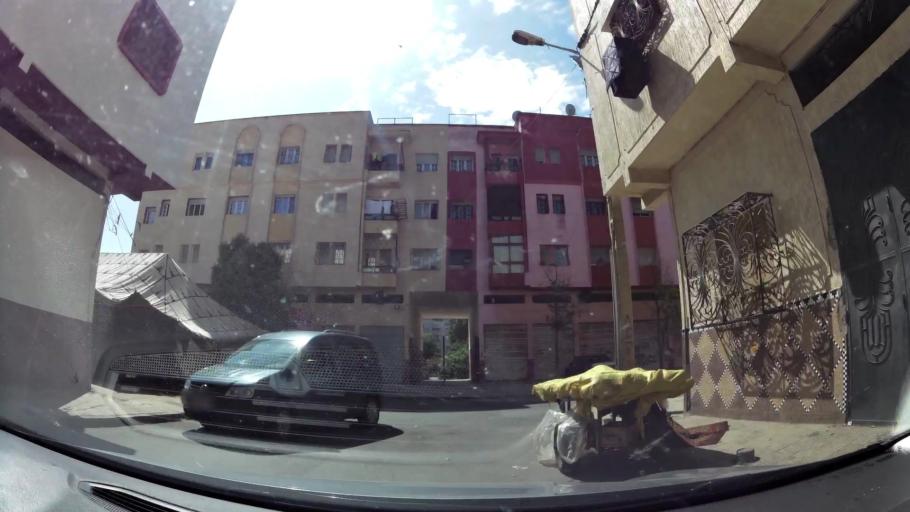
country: MA
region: Rabat-Sale-Zemmour-Zaer
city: Sale
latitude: 34.0618
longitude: -6.8030
